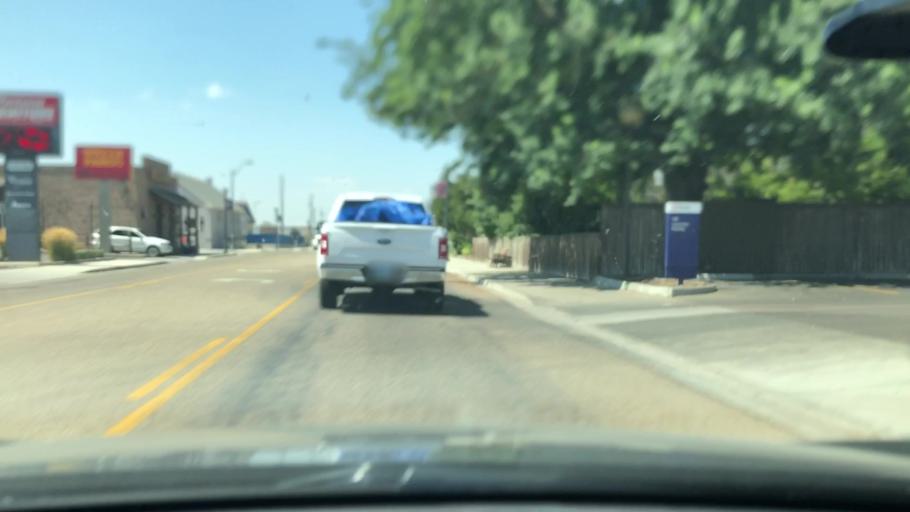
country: US
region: Idaho
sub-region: Canyon County
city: Parma
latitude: 43.7858
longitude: -116.9443
